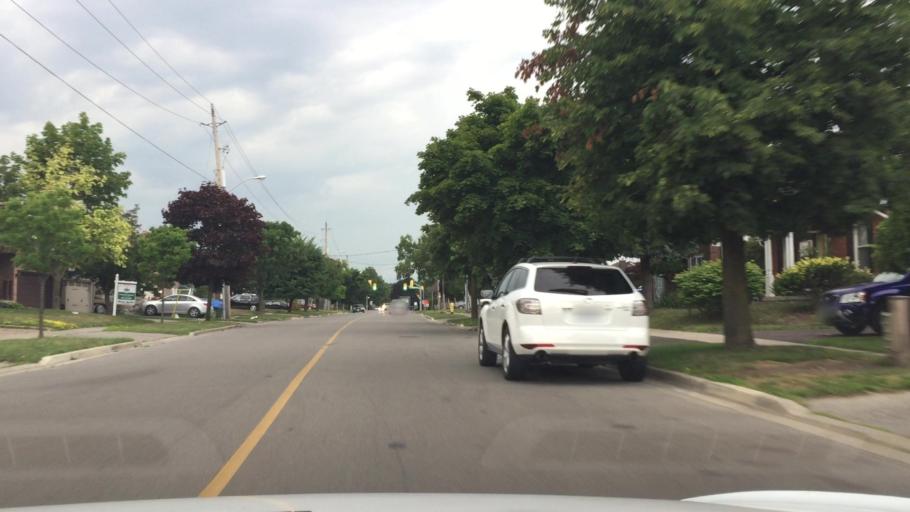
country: CA
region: Ontario
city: Oshawa
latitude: 43.9091
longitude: -78.8037
